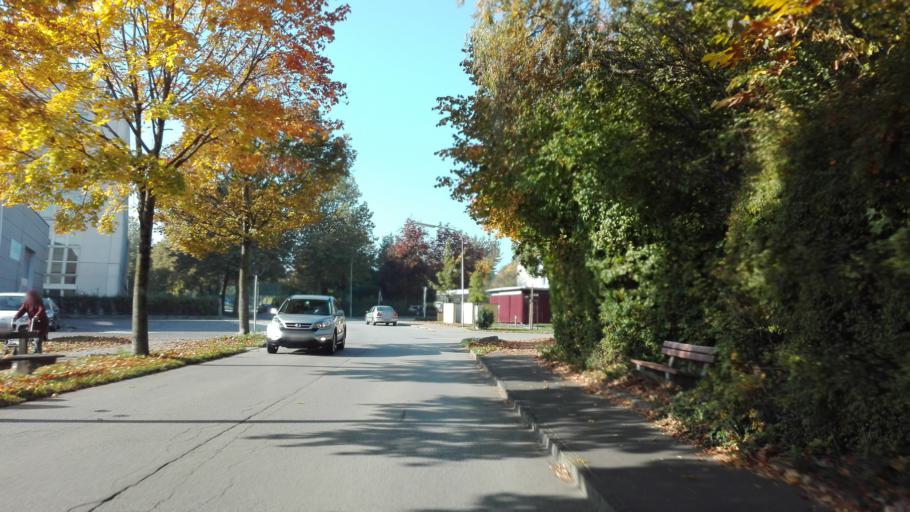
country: AT
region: Upper Austria
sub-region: Politischer Bezirk Linz-Land
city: Leonding
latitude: 48.2667
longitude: 14.2612
